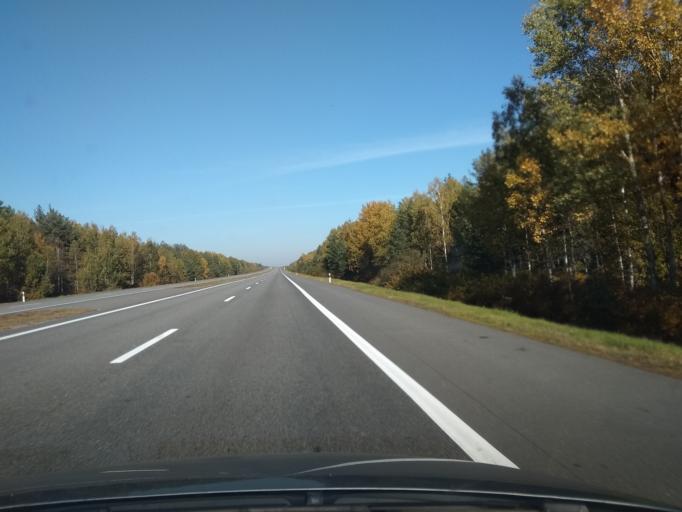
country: BY
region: Grodnenskaya
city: Zhyrovichy
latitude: 52.9003
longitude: 25.6752
